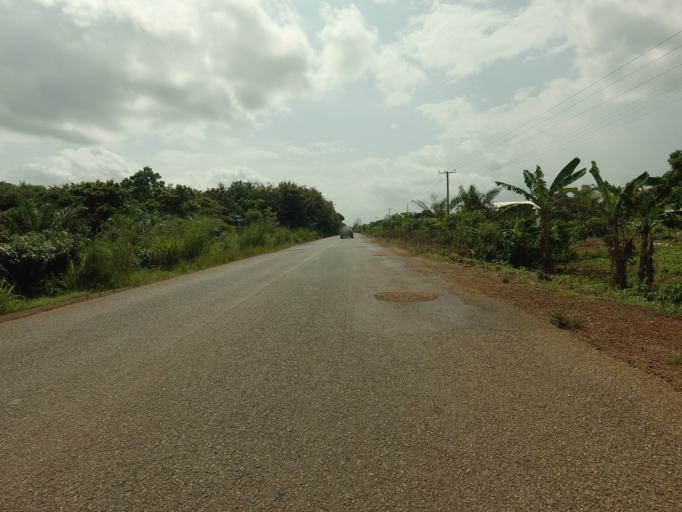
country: TG
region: Maritime
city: Lome
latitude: 6.2155
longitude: 1.0470
